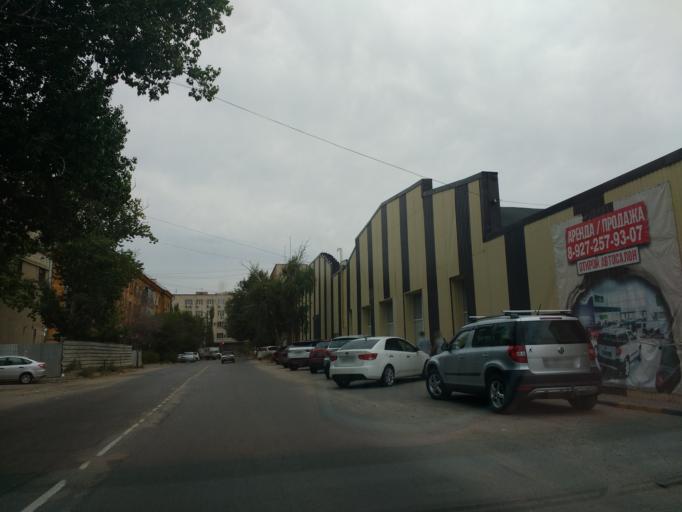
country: RU
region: Volgograd
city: Volgograd
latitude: 48.6948
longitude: 44.4873
